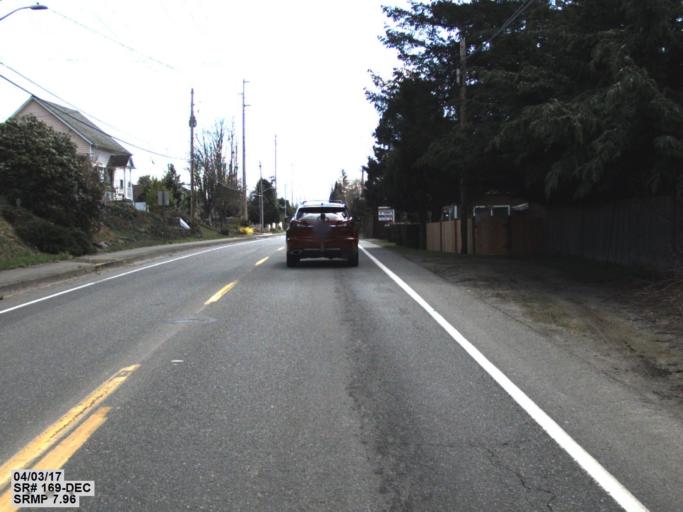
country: US
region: Washington
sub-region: King County
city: Black Diamond
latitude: 47.3133
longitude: -122.0048
